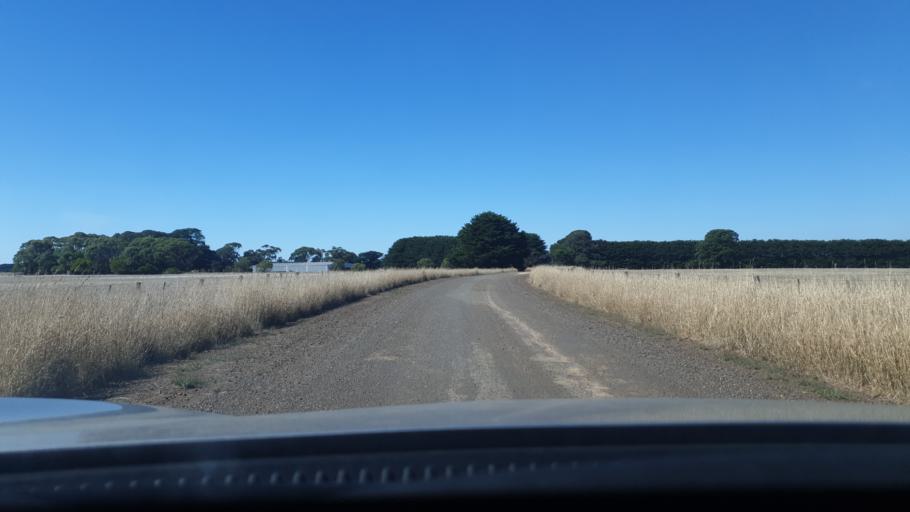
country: AU
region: Victoria
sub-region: Warrnambool
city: Warrnambool
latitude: -38.1652
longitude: 142.3722
